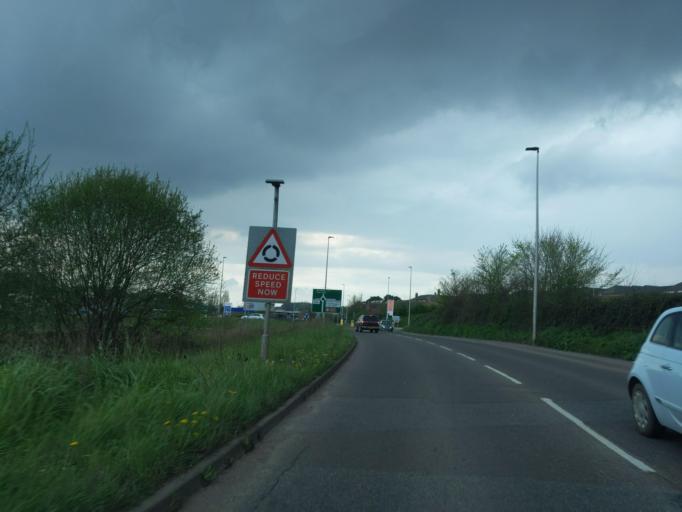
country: GB
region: England
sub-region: Devon
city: Crediton
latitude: 50.7843
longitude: -3.6376
